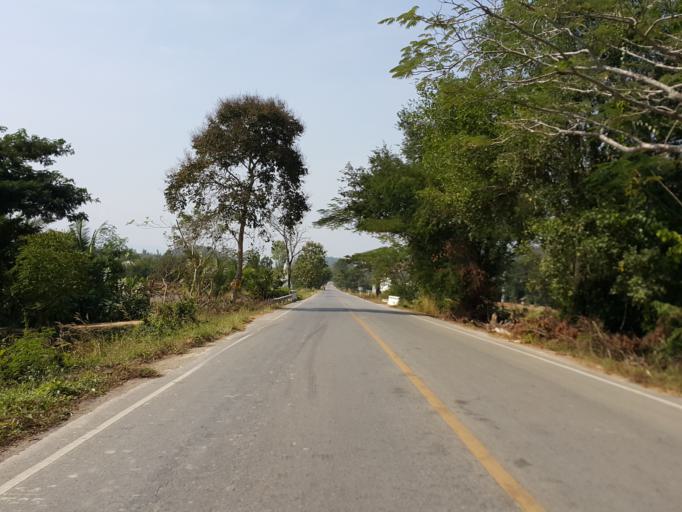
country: TH
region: Sukhothai
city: Thung Saliam
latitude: 17.3350
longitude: 99.4874
